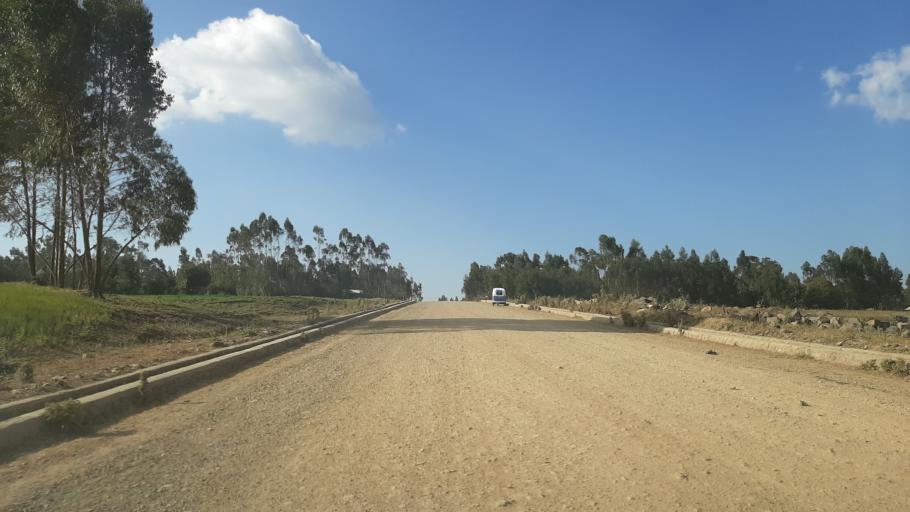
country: ET
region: Amhara
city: Dabat
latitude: 12.9967
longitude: 37.7636
